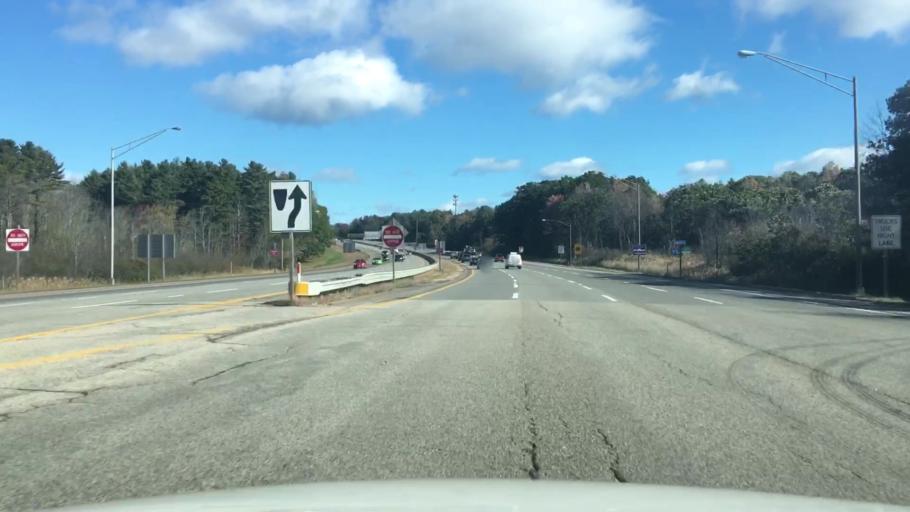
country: US
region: Maine
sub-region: York County
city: York Harbor
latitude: 43.1615
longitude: -70.6574
